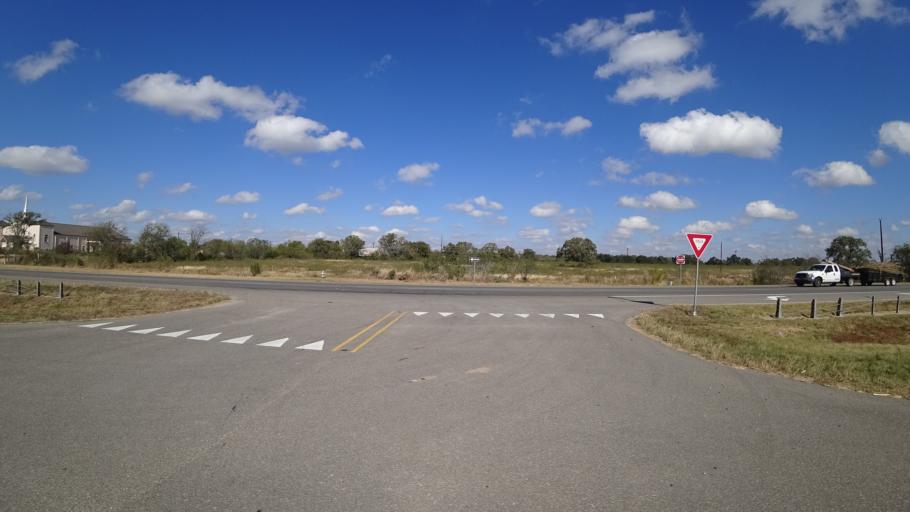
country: US
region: Texas
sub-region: Travis County
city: Garfield
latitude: 30.1870
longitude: -97.6024
